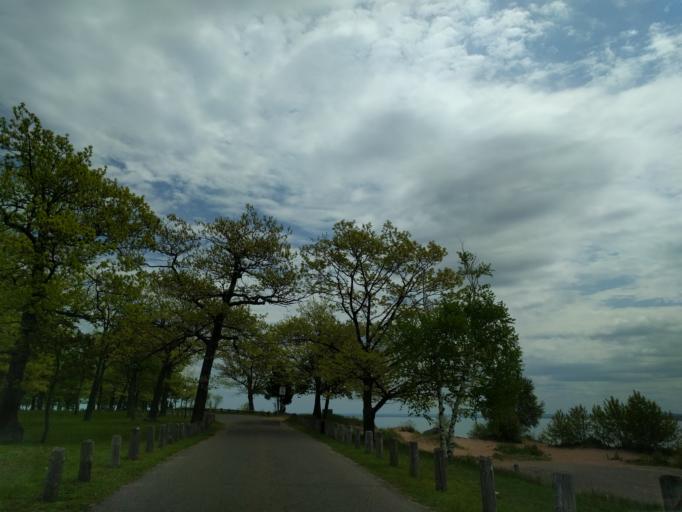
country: US
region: Michigan
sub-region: Marquette County
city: Marquette
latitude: 46.5814
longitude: -87.3837
